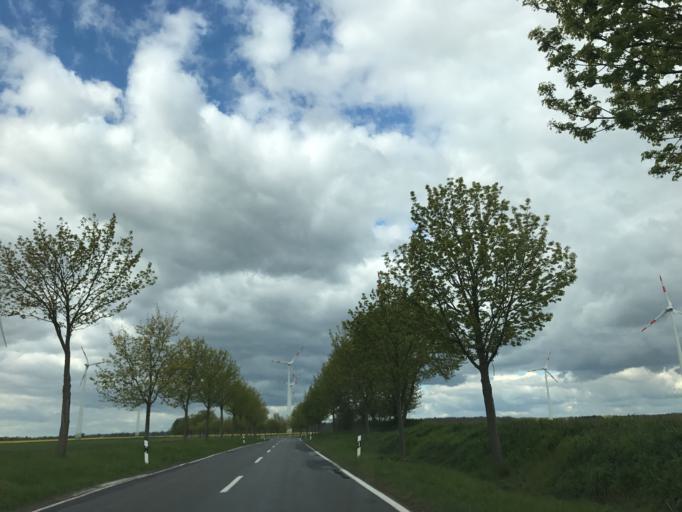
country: DE
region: Brandenburg
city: Nauen
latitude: 52.5913
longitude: 12.8068
